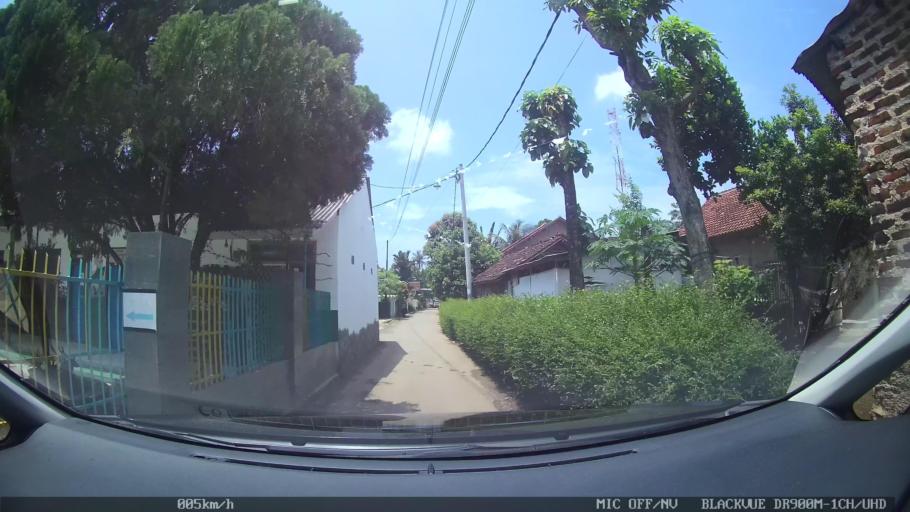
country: ID
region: Lampung
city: Kedaton
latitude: -5.3554
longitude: 105.2890
